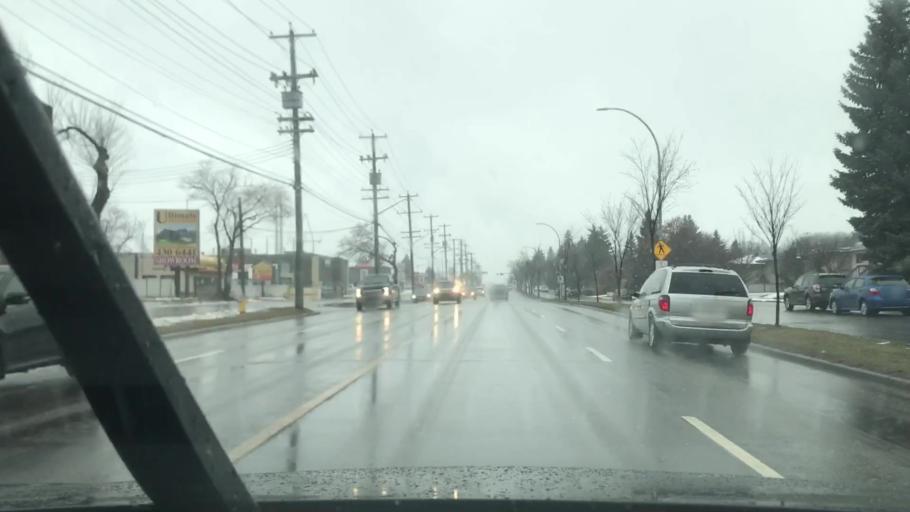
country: CA
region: Alberta
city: Edmonton
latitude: 53.4999
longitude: -113.4746
